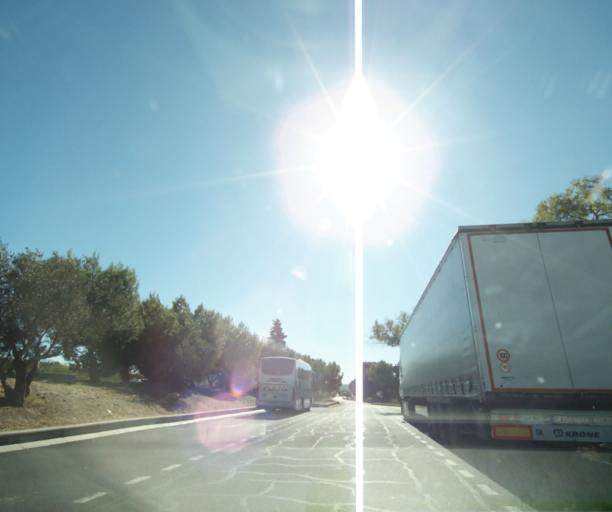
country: FR
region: Languedoc-Roussillon
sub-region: Departement de l'Herault
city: Lespignan
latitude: 43.2655
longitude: 3.1747
